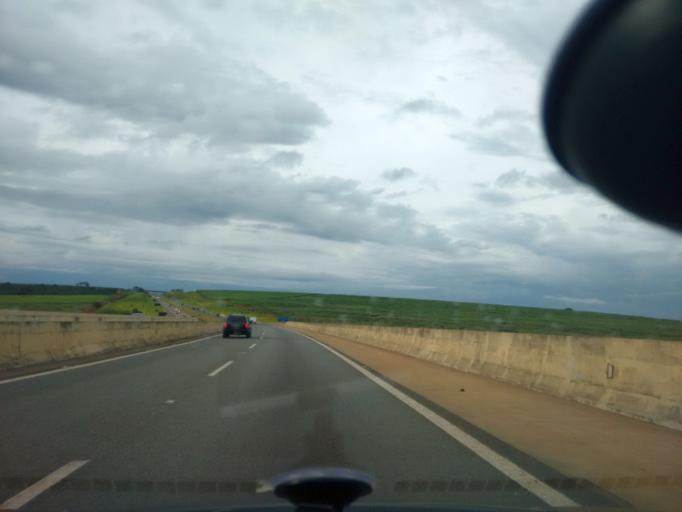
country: BR
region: Sao Paulo
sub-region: Cordeiropolis
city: Cordeiropolis
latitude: -22.5203
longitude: -47.4319
